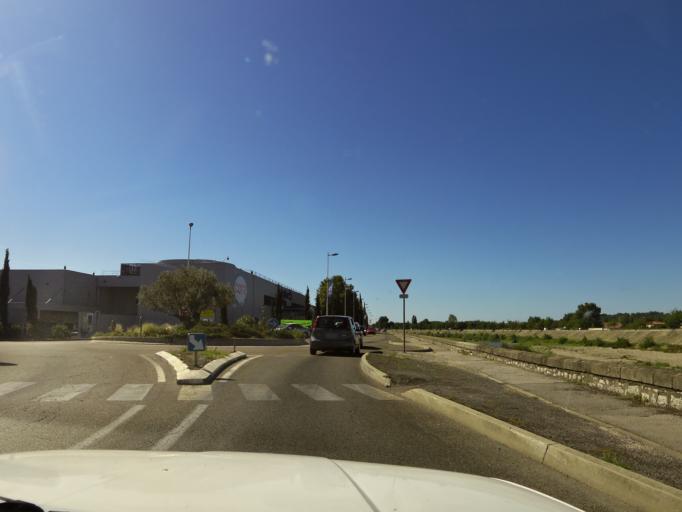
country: FR
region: Languedoc-Roussillon
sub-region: Departement du Gard
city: Ales
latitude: 44.1150
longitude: 4.0958
